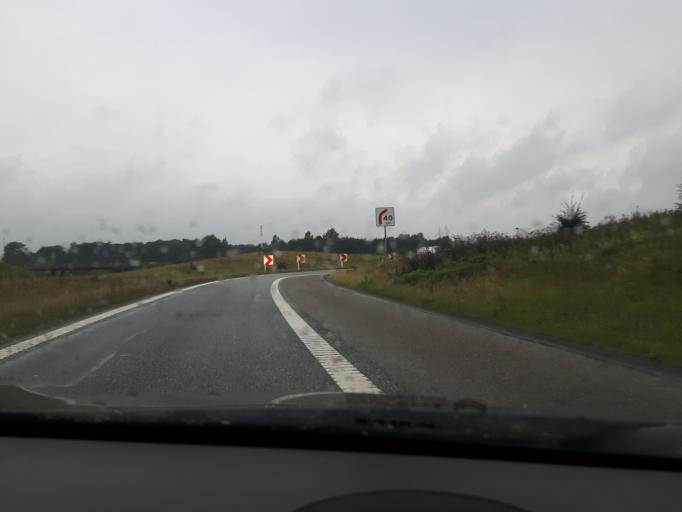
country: DK
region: Central Jutland
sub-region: Arhus Kommune
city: Framlev
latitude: 56.1558
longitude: 10.0473
